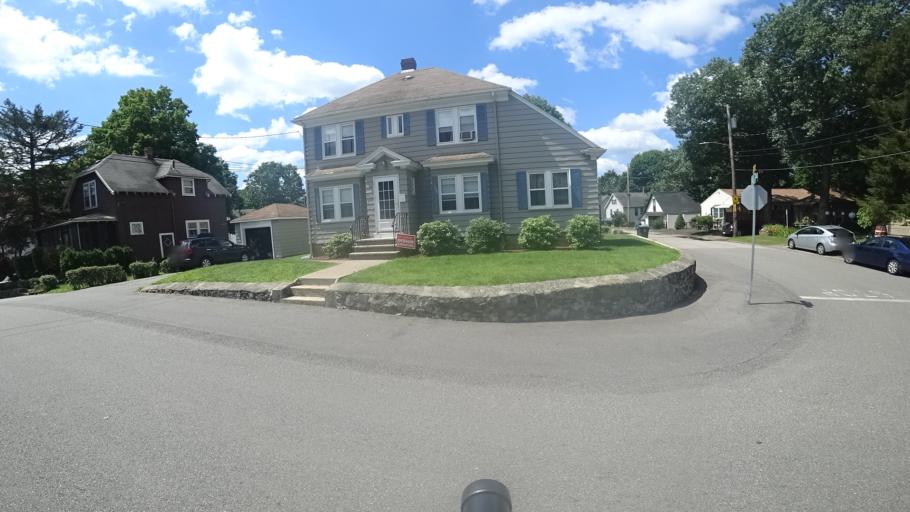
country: US
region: Massachusetts
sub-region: Norfolk County
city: Dedham
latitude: 42.2567
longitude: -71.1612
